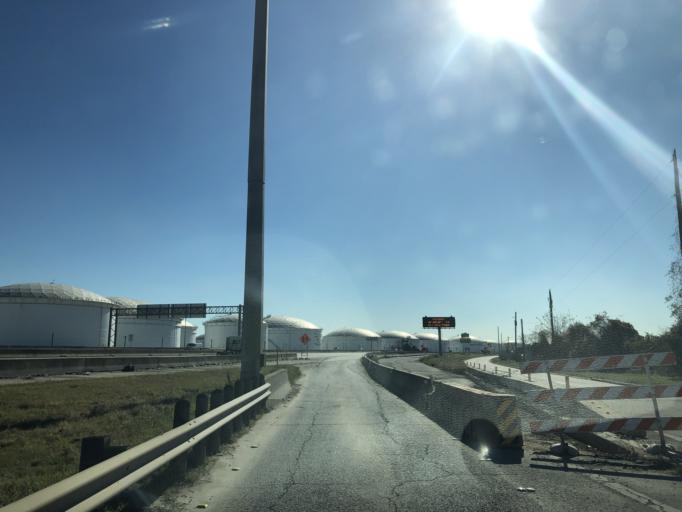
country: US
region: Texas
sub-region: Harris County
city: Cloverleaf
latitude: 29.7655
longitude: -95.1494
